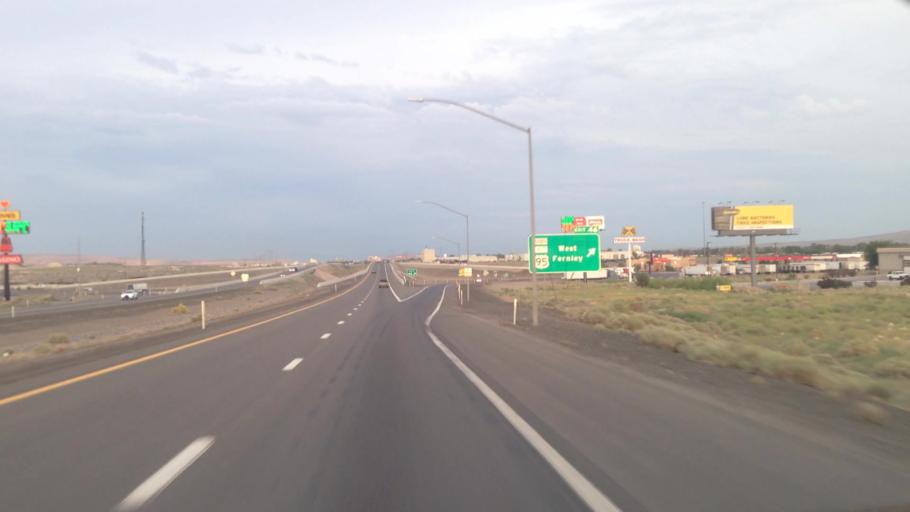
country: US
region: Nevada
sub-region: Lyon County
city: Fernley
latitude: 39.6167
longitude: -119.2712
